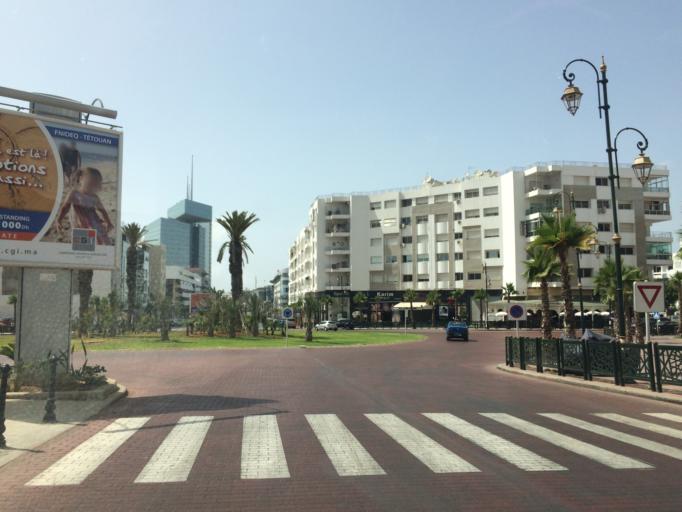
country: MA
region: Rabat-Sale-Zemmour-Zaer
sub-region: Skhirate-Temara
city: Temara
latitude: 33.9554
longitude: -6.8663
